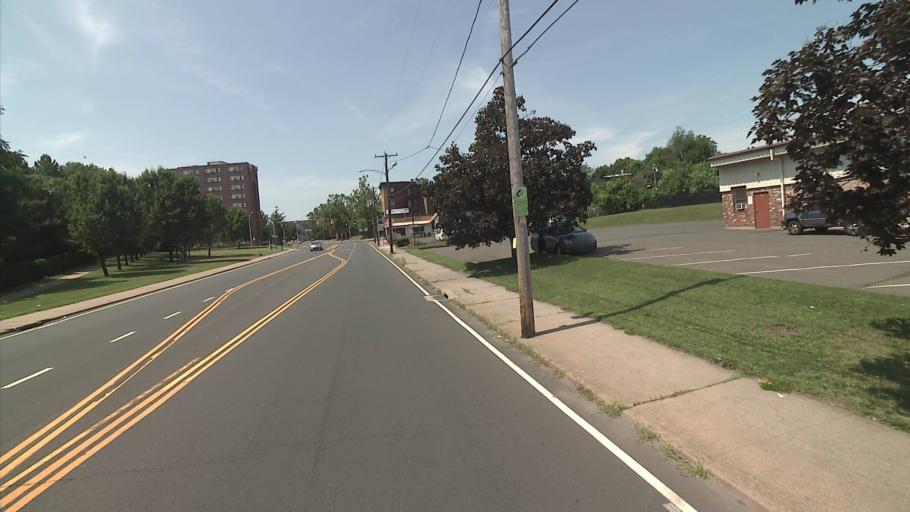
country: US
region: Connecticut
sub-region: Hartford County
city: New Britain
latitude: 41.6745
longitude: -72.7726
